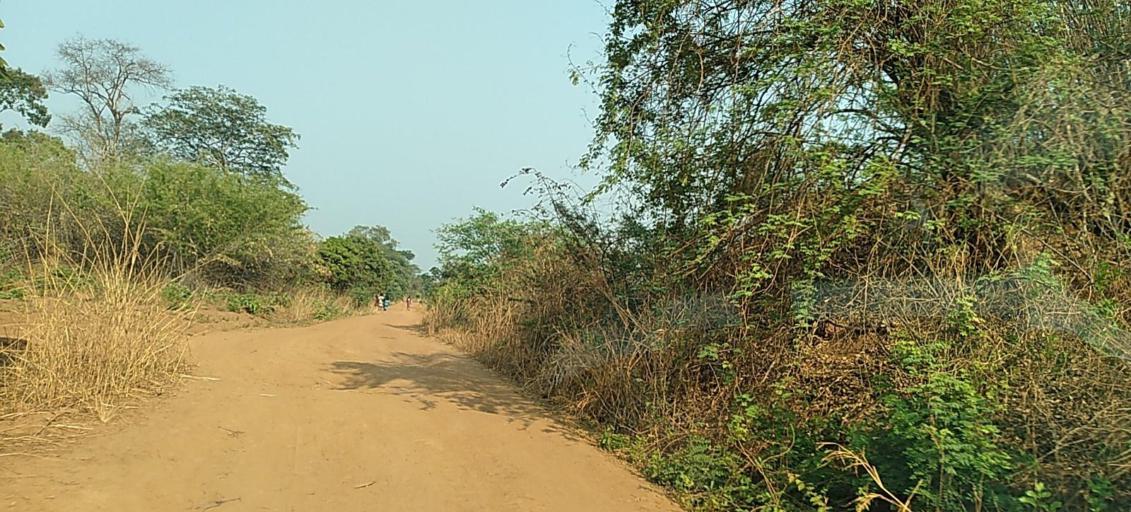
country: ZM
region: Copperbelt
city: Chingola
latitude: -12.8546
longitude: 27.5567
